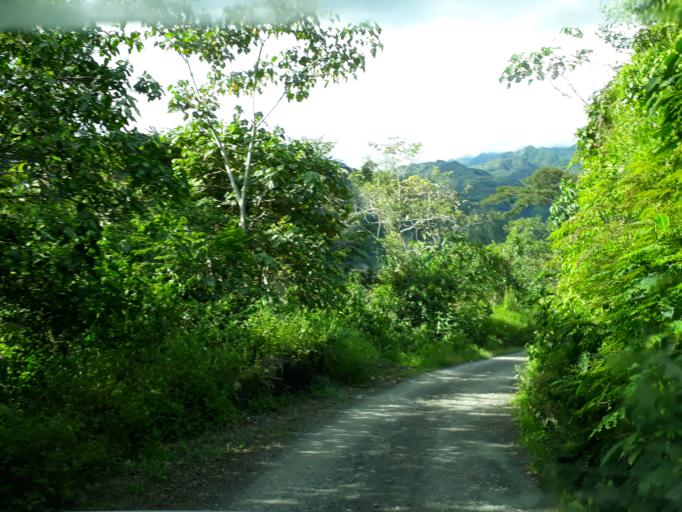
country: CO
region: Cundinamarca
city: Pacho
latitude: 5.1899
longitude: -74.2488
